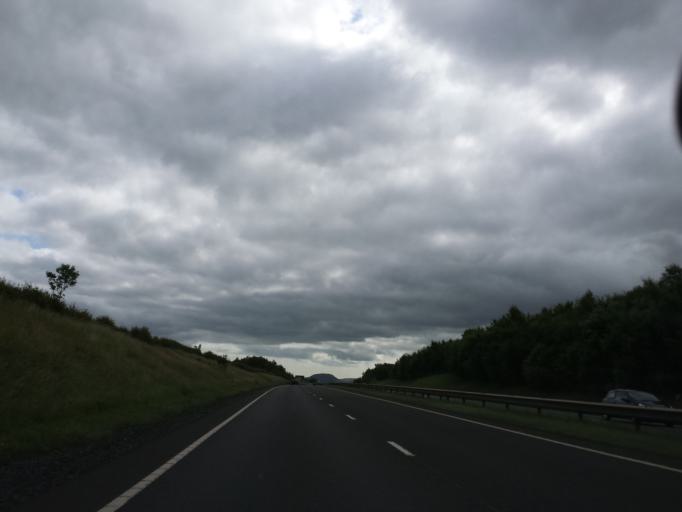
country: GB
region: Scotland
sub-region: East Lothian
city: Longniddry
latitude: 55.9537
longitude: -2.8475
